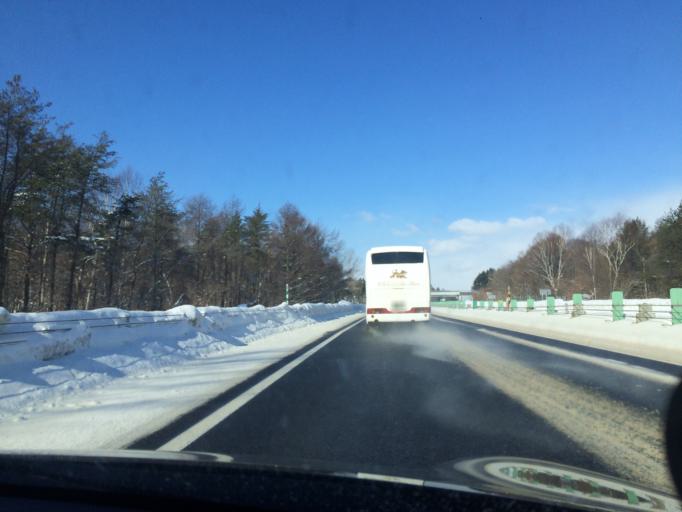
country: JP
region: Hokkaido
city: Chitose
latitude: 42.8549
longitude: 141.5643
